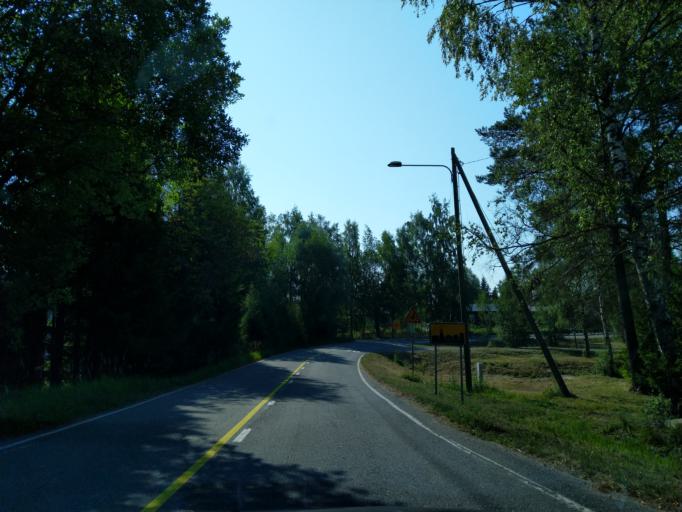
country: FI
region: Satakunta
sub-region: Pori
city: Pomarkku
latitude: 61.7072
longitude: 22.0276
